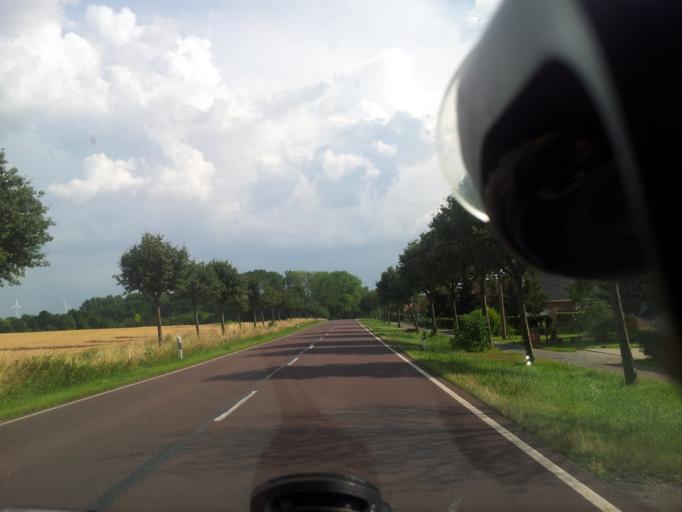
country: DE
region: Saxony-Anhalt
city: Gross Bornecke
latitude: 51.8220
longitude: 11.4567
